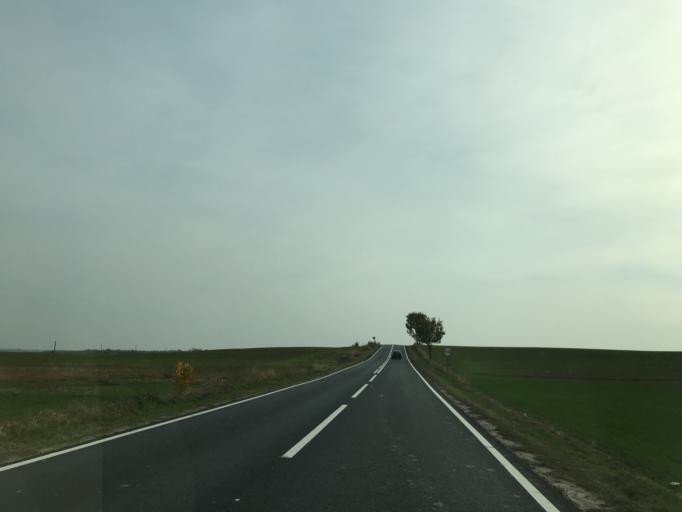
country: RO
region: Olt
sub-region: Comuna Brancoveni
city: Brancoveni
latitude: 44.3322
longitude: 24.2969
